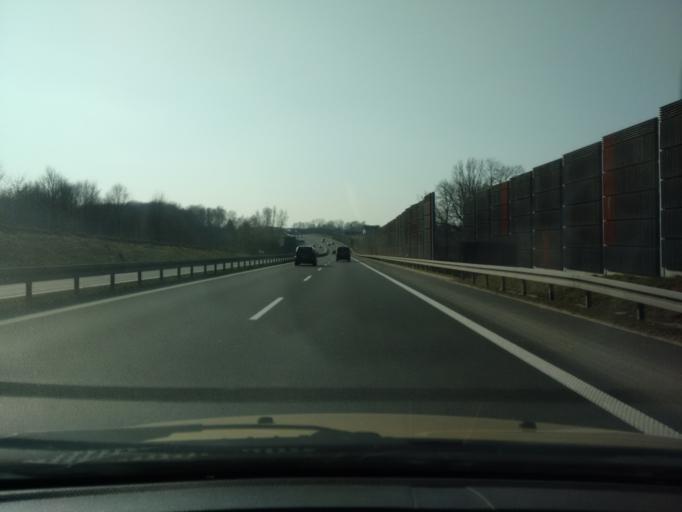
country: PL
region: Silesian Voivodeship
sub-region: Bielsko-Biala
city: Bielsko-Biala
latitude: 49.8474
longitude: 19.0193
